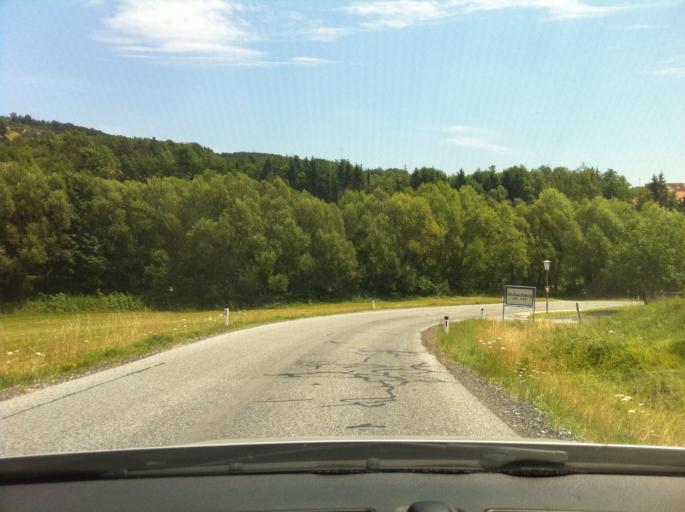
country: AT
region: Styria
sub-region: Politischer Bezirk Hartberg-Fuerstenfeld
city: Stubenberg
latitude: 47.2472
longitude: 15.7963
